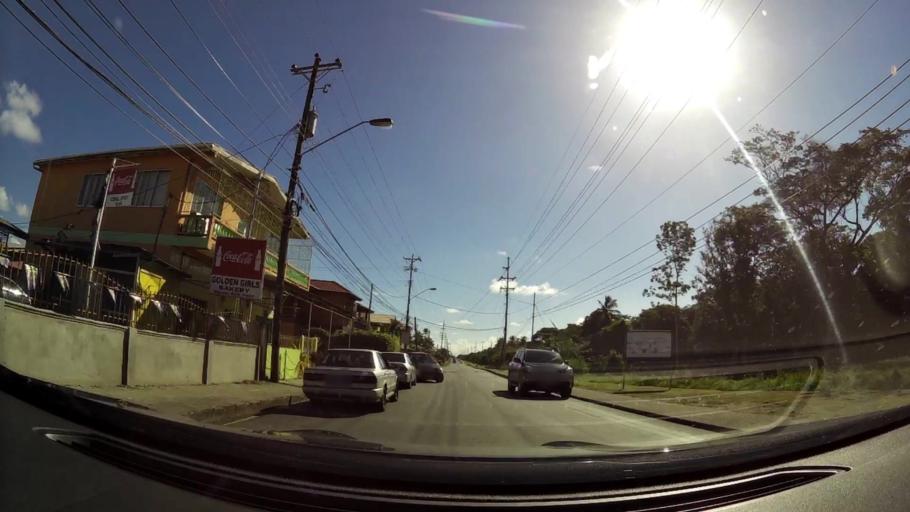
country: TT
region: Tobago
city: Scarborough
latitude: 11.1564
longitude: -60.8074
